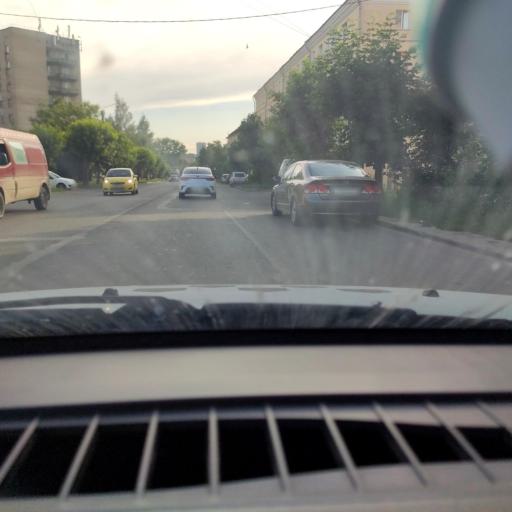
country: RU
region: Kirov
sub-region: Kirovo-Chepetskiy Rayon
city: Kirov
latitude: 58.6237
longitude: 49.6445
